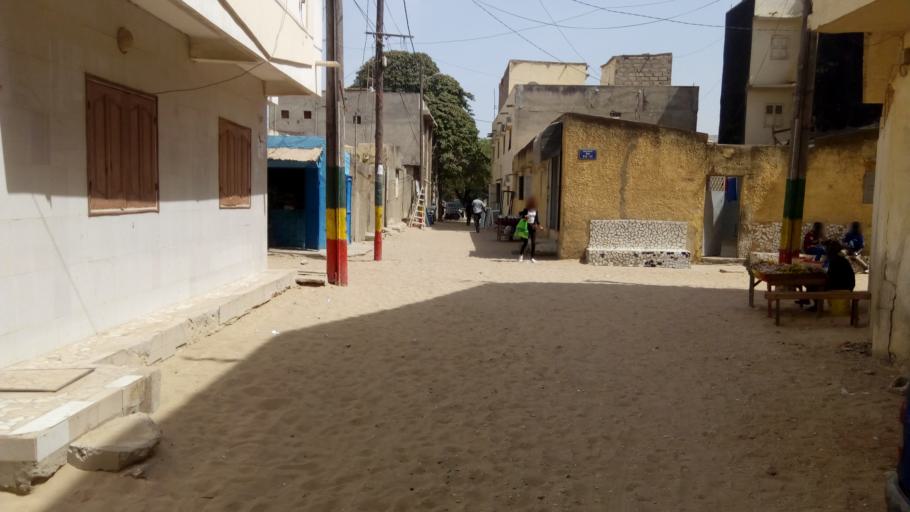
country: SN
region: Dakar
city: Grand Dakar
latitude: 14.7131
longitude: -17.4471
